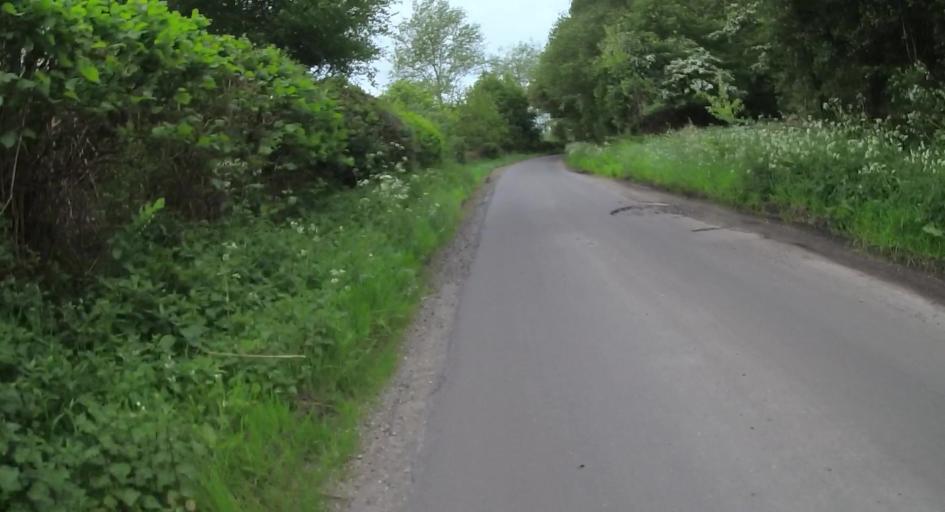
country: GB
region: England
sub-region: West Berkshire
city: Stratfield Mortimer
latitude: 51.3532
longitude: -1.0651
